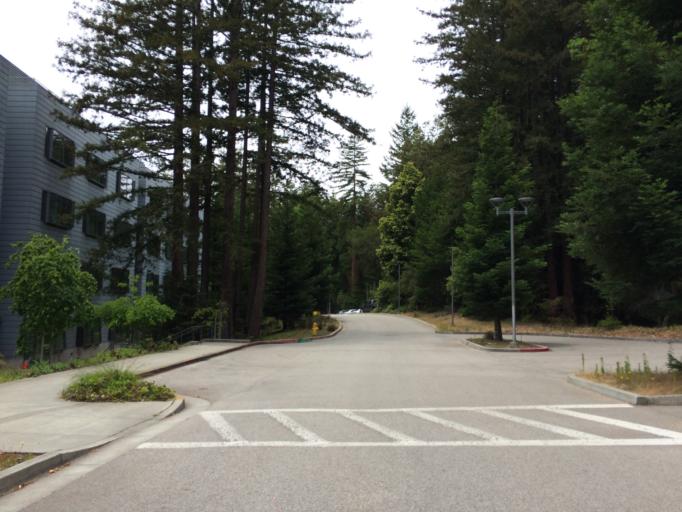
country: US
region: California
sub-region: Santa Cruz County
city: Pasatiempo
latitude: 37.0014
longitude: -122.0628
